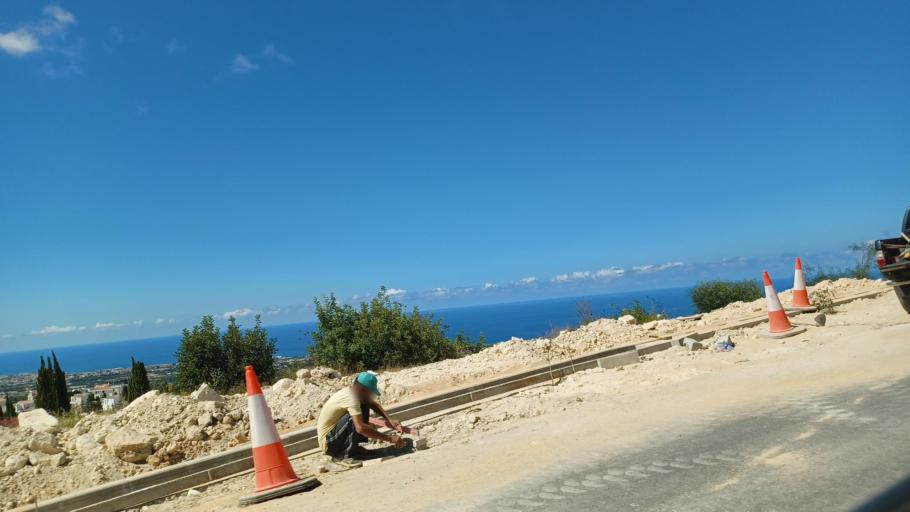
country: CY
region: Pafos
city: Tala
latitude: 34.8450
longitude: 32.4329
